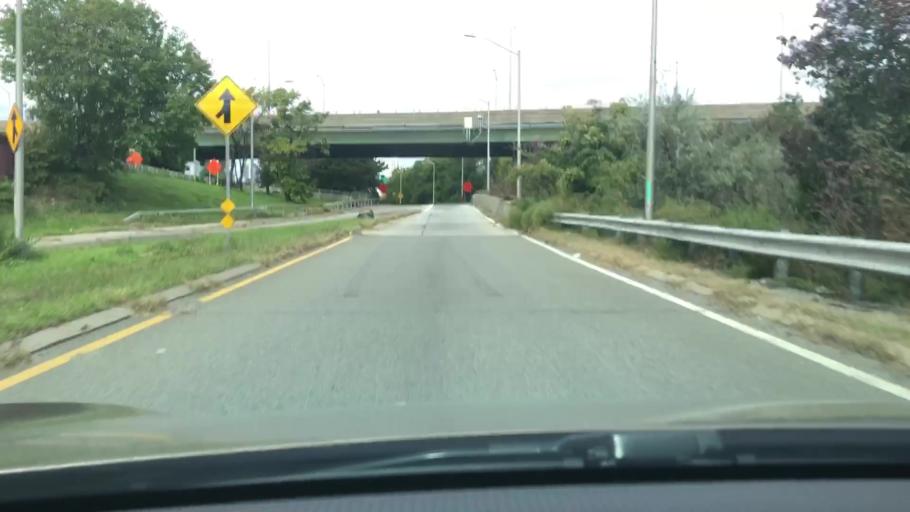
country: US
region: New York
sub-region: Queens County
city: Long Island City
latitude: 40.7340
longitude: -73.9212
